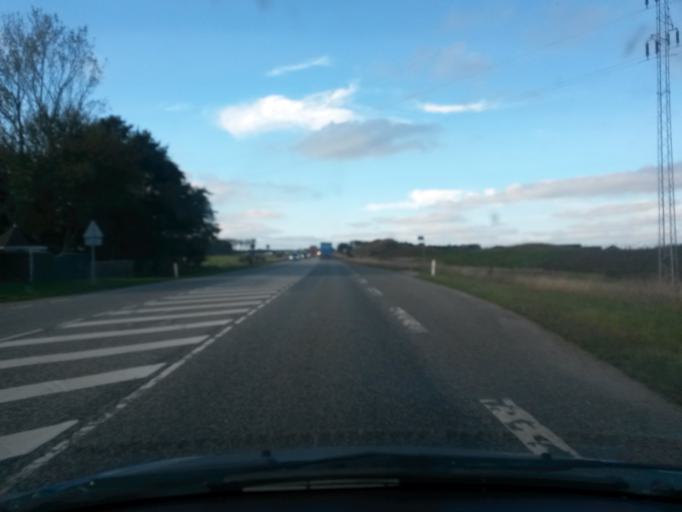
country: DK
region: Central Jutland
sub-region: Holstebro Kommune
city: Holstebro
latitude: 56.3297
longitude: 8.6588
